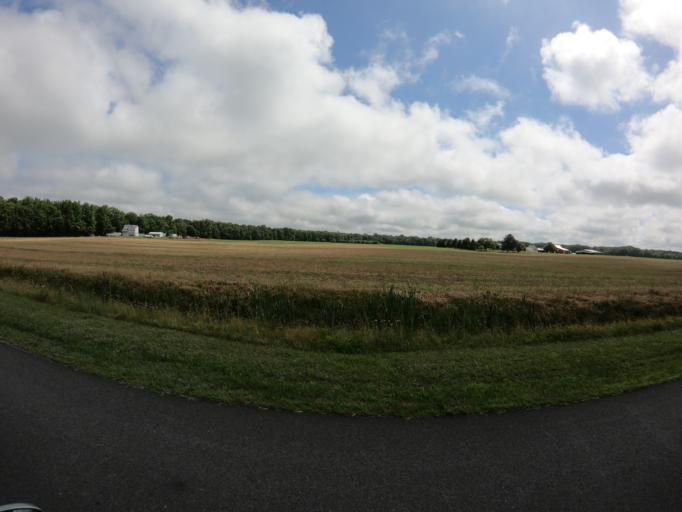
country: US
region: Maryland
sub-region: Caroline County
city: Greensboro
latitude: 39.0493
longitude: -75.8320
